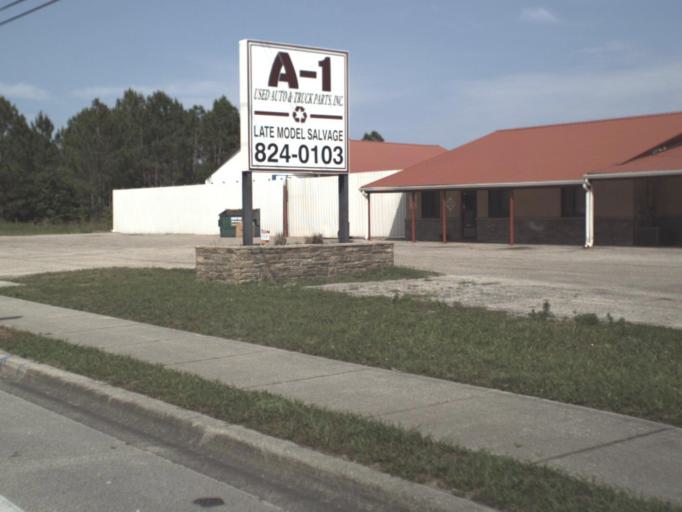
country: US
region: Florida
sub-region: Saint Johns County
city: Saint Augustine South
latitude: 29.8552
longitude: -81.3542
